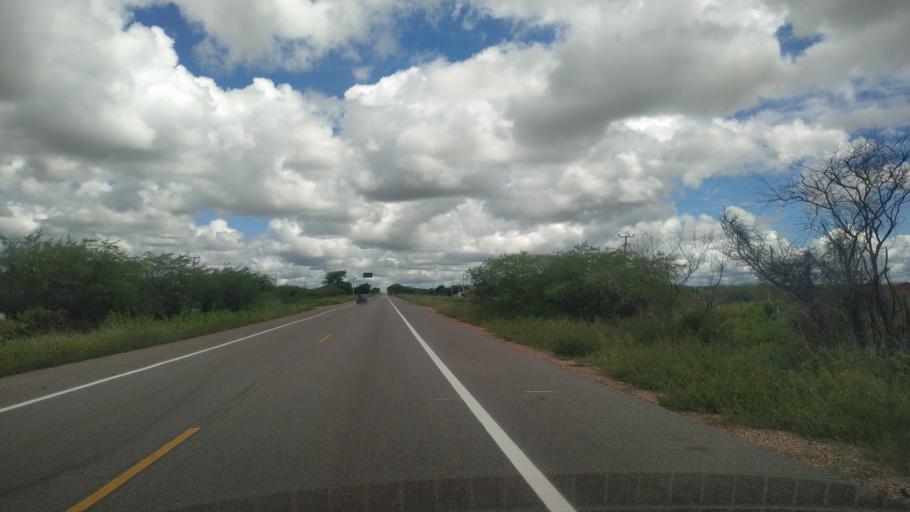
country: BR
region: Rio Grande do Norte
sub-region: Areia Branca
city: Areia Branca
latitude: -5.0541
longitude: -37.1522
